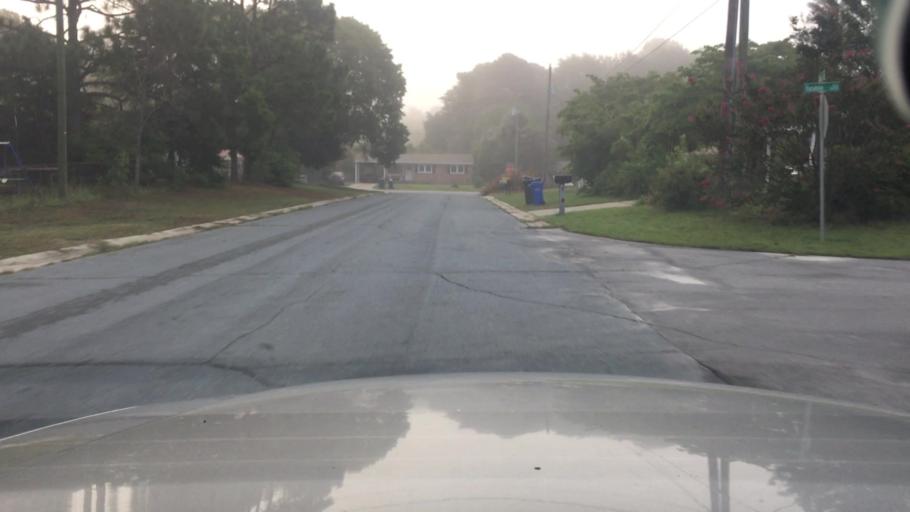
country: US
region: North Carolina
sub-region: Cumberland County
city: Hope Mills
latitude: 35.0181
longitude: -78.9260
